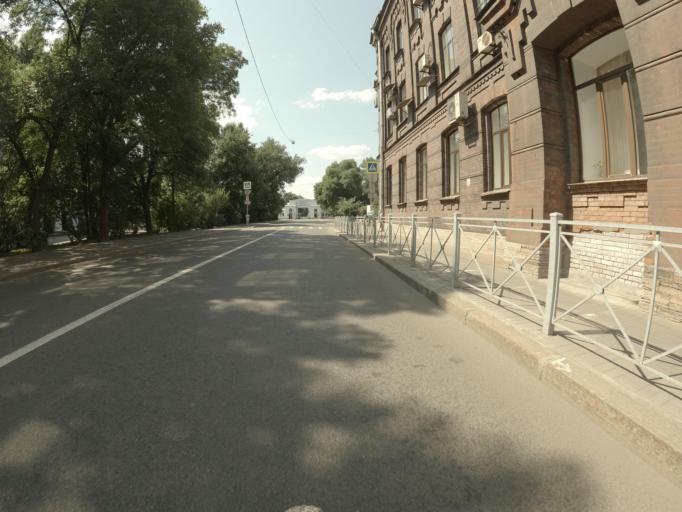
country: RU
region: St.-Petersburg
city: Vasyl'evsky Ostrov
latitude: 59.9108
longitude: 30.2511
